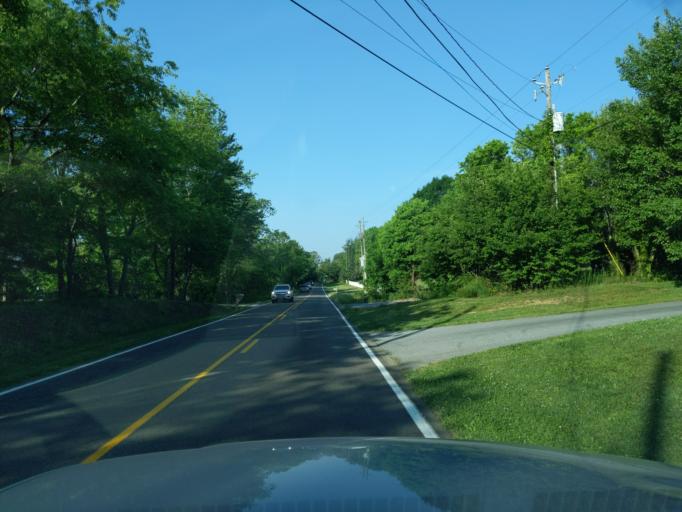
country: US
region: North Carolina
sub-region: Henderson County
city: Hoopers Creek
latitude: 35.4580
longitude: -82.4711
